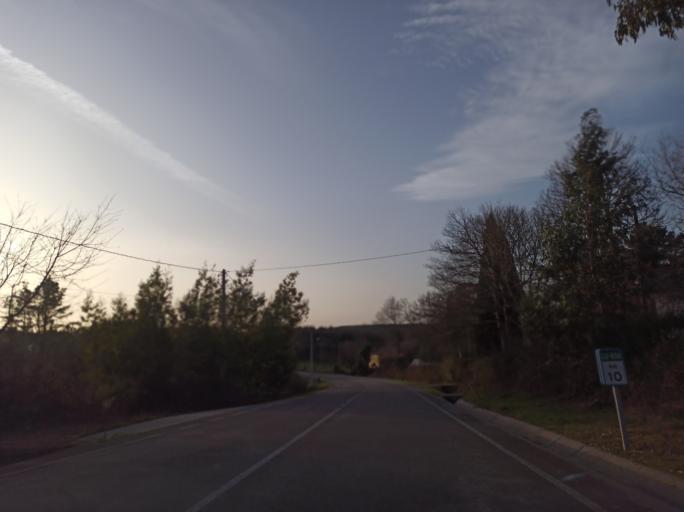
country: ES
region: Galicia
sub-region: Provincia de Lugo
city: Friol
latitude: 43.0358
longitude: -7.8963
